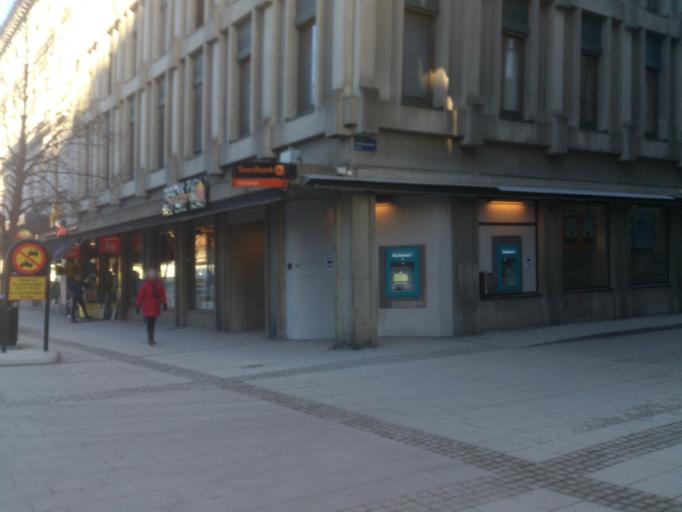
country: SE
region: Vaesternorrland
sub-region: Sundsvalls Kommun
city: Sundsvall
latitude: 62.3909
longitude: 17.3104
